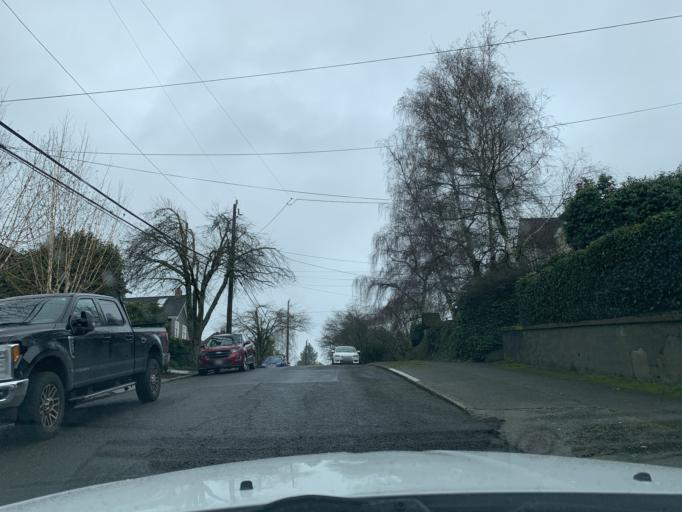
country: US
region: Washington
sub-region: King County
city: Seattle
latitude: 47.6059
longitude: -122.2905
